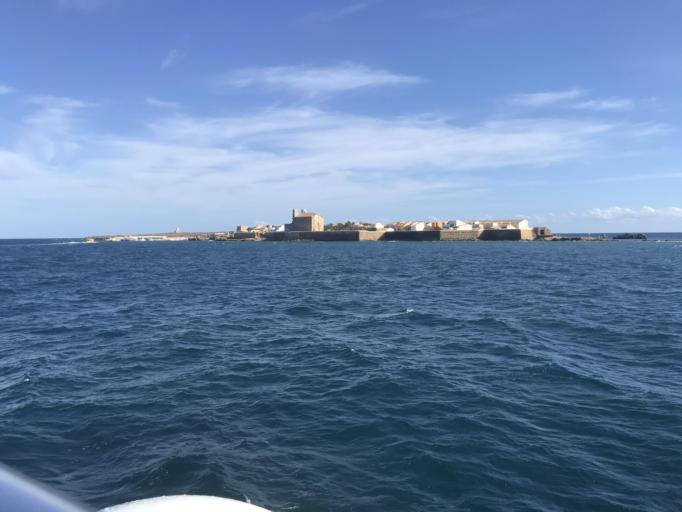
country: ES
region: Valencia
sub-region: Provincia de Alicante
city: Santa Pola
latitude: 38.1700
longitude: -0.4865
